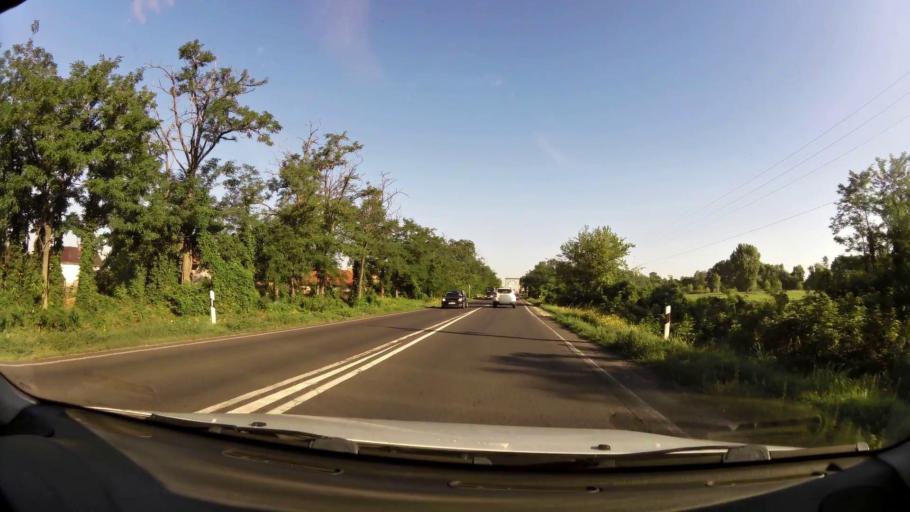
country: HU
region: Pest
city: Pilis
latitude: 47.2792
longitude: 19.5550
